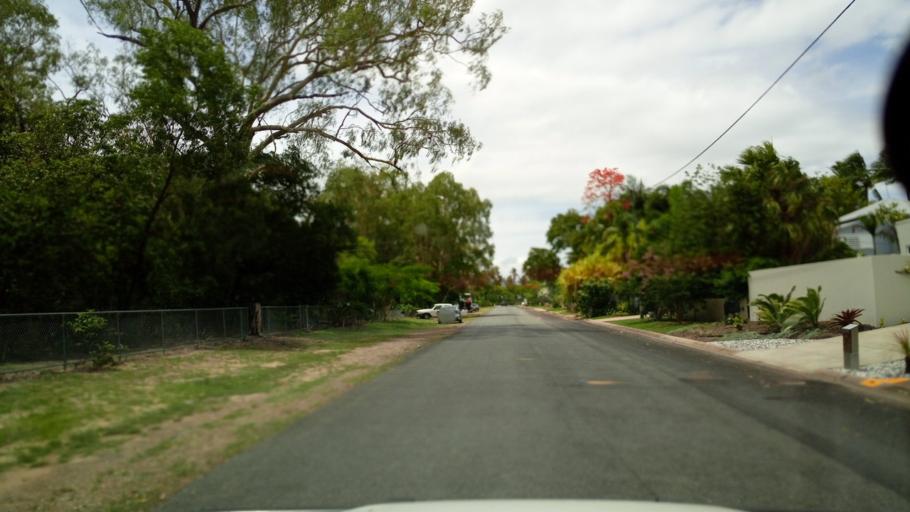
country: AU
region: Queensland
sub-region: Cairns
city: Redlynch
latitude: -16.8587
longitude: 145.7562
